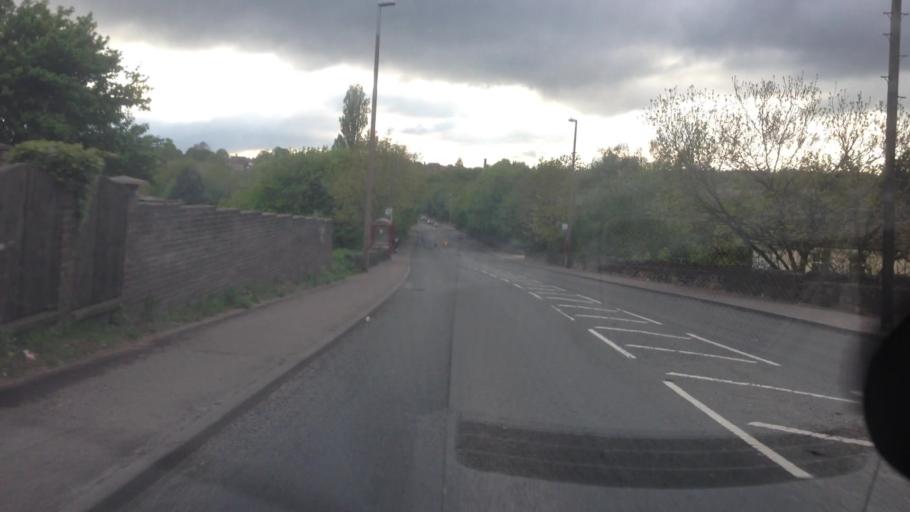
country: GB
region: England
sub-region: City and Borough of Wakefield
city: Ossett
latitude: 53.6917
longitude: -1.5986
